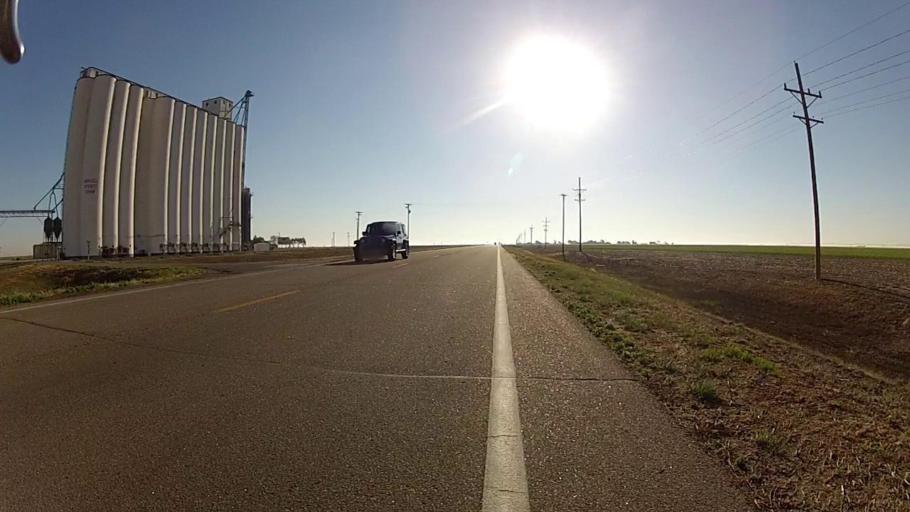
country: US
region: Kansas
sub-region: Haskell County
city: Sublette
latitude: 37.4874
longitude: -100.8288
